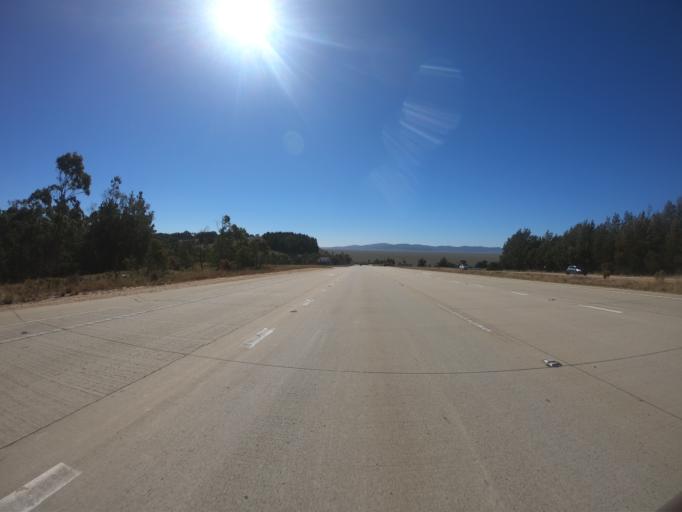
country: AU
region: New South Wales
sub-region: Yass Valley
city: Gundaroo
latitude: -35.1018
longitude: 149.3738
